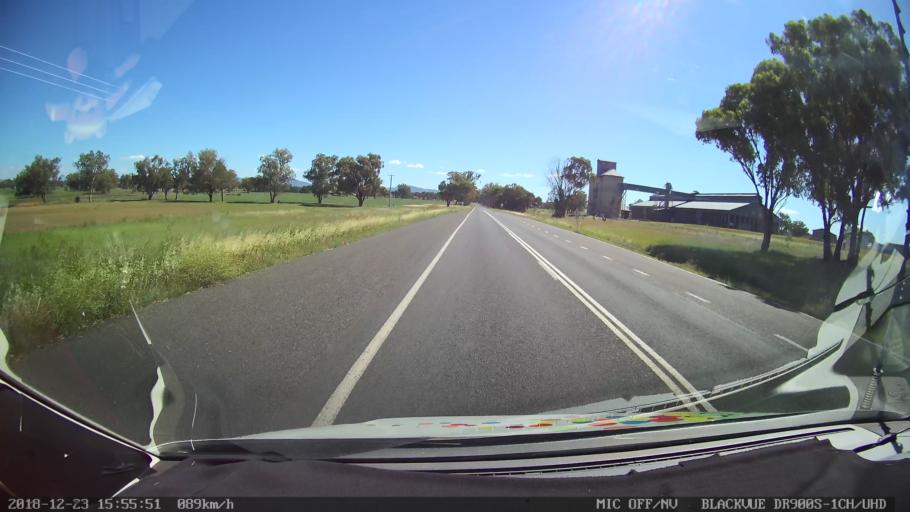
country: AU
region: New South Wales
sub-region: Tamworth Municipality
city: Phillip
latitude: -31.1597
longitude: 150.8642
